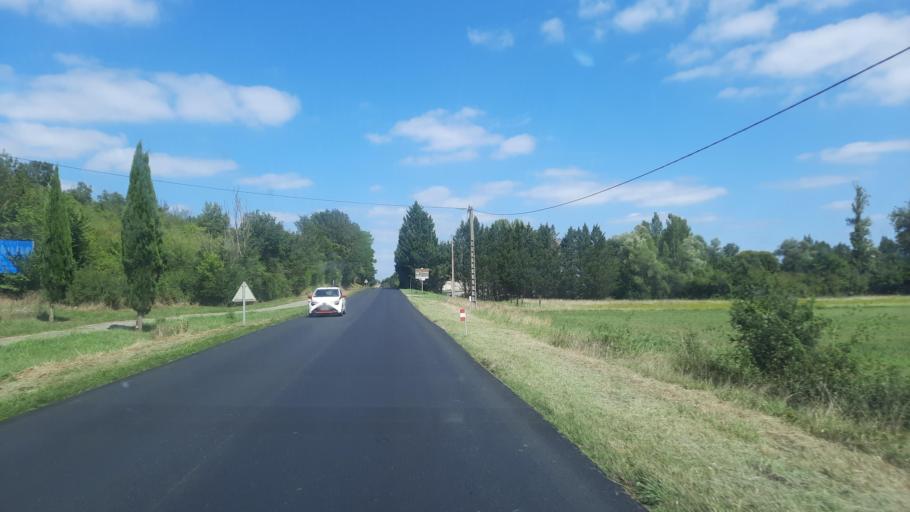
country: FR
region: Midi-Pyrenees
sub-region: Departement du Gers
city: Lombez
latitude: 43.4698
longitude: 0.8981
